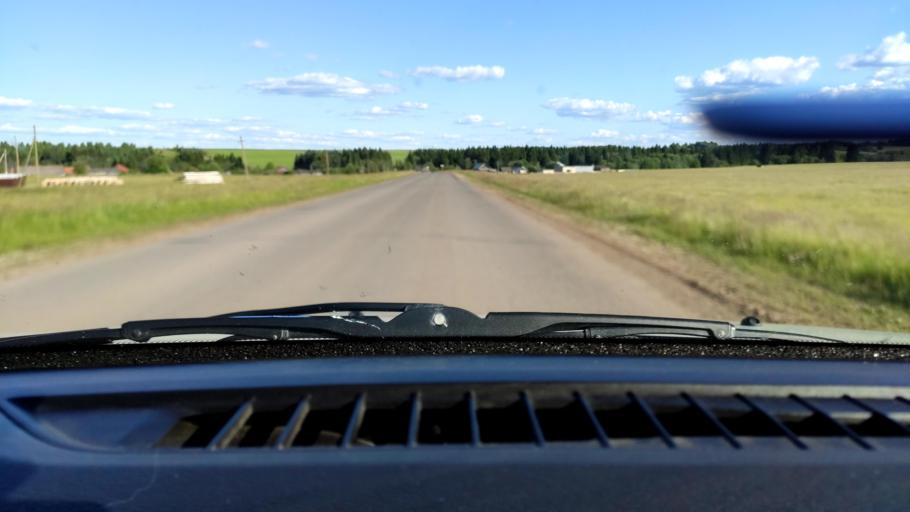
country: RU
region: Perm
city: Uinskoye
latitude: 57.0767
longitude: 56.5574
